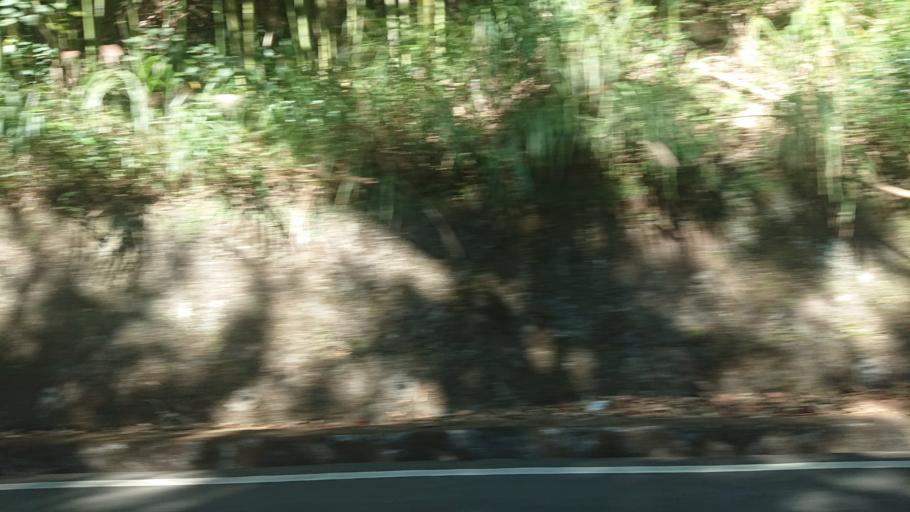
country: TW
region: Taiwan
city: Lugu
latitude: 23.4901
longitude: 120.7531
